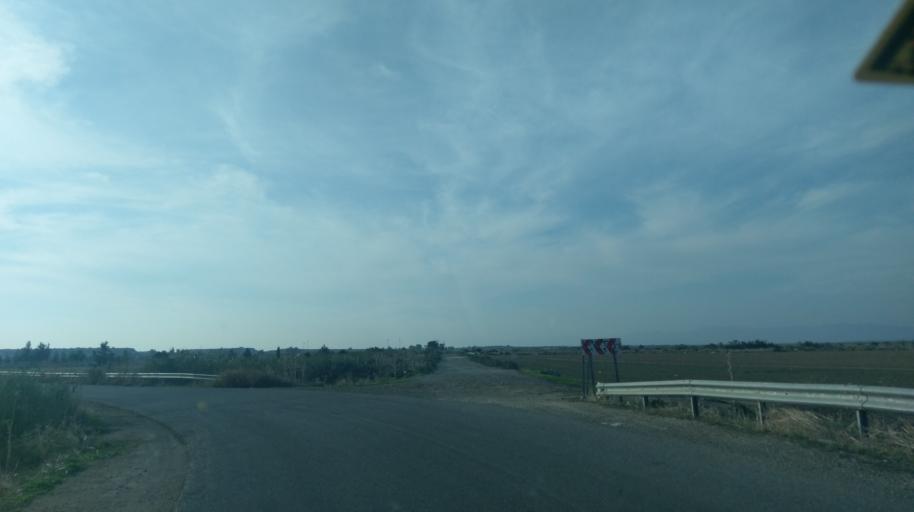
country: CY
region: Ammochostos
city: Achna
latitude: 35.1001
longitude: 33.8060
